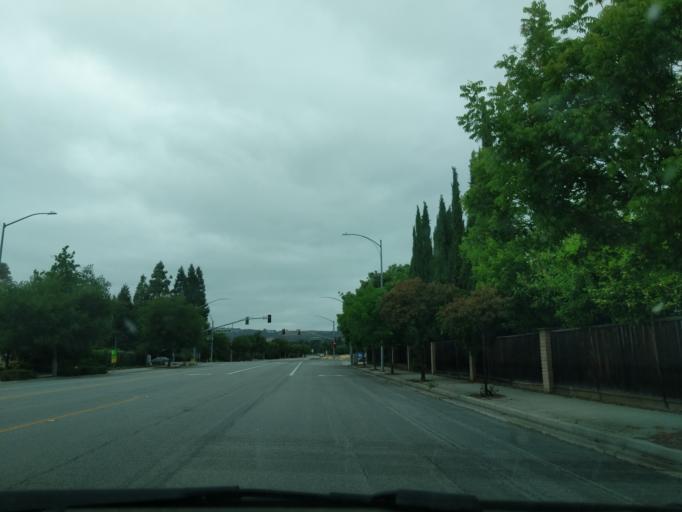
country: US
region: California
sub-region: Santa Clara County
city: Morgan Hill
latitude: 37.1376
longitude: -121.6148
